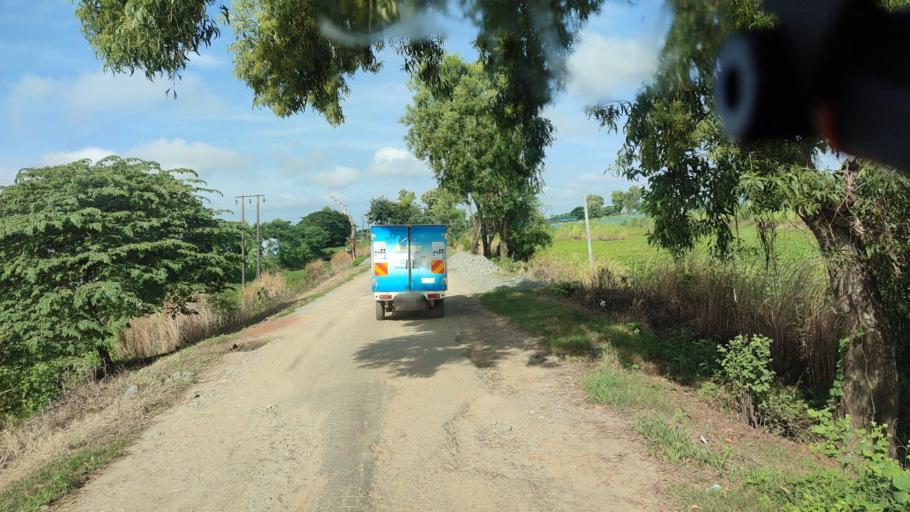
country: MM
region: Bago
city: Letpandan
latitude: 17.7689
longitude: 95.6984
